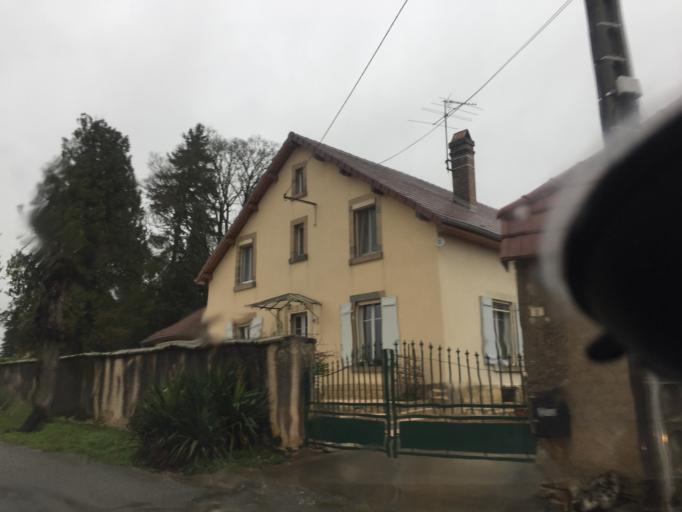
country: FR
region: Franche-Comte
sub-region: Departement du Jura
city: Orchamps
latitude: 47.1561
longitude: 5.6269
